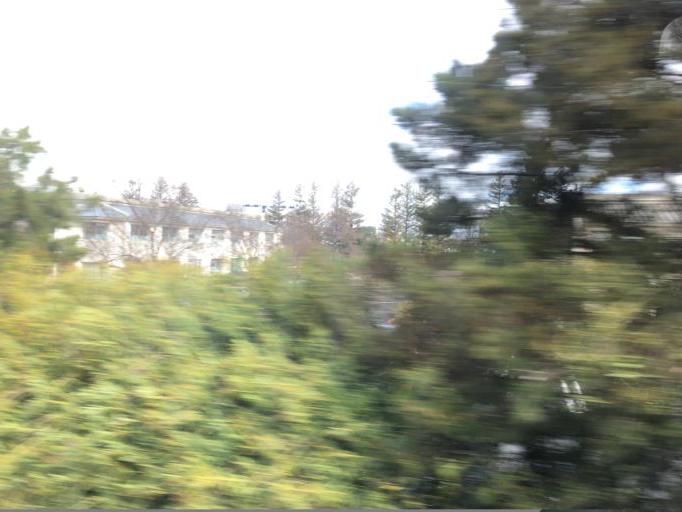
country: US
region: California
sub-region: Santa Clara County
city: Santa Clara
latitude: 37.3691
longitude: -121.9722
